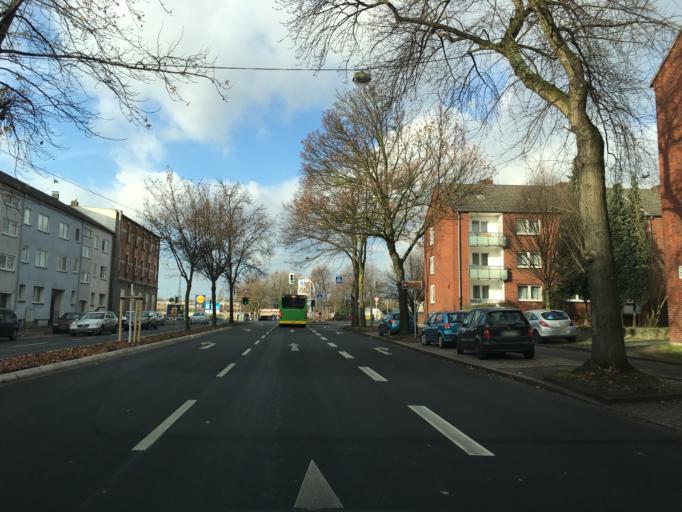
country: DE
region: North Rhine-Westphalia
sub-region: Regierungsbezirk Dusseldorf
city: Oberhausen
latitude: 51.4771
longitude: 6.8413
